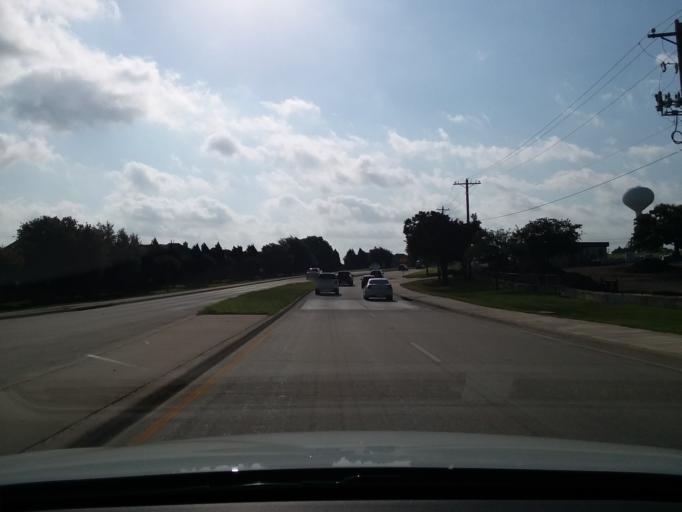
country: US
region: Texas
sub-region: Denton County
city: Double Oak
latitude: 33.0739
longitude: -97.1172
